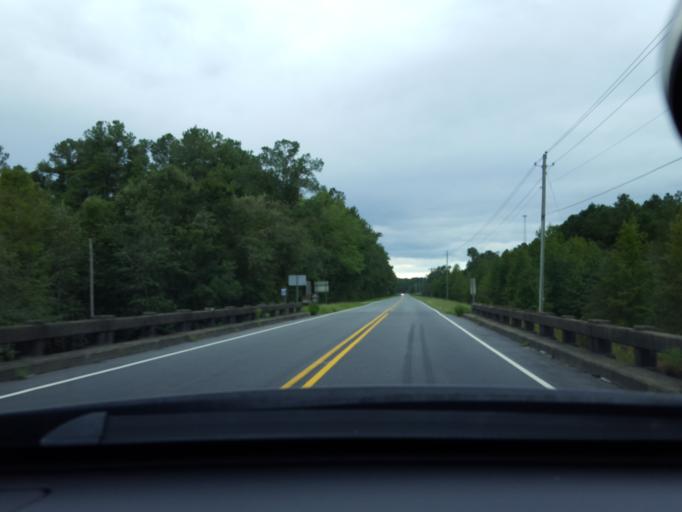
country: US
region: North Carolina
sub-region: Sampson County
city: Roseboro
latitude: 34.7616
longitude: -78.4088
